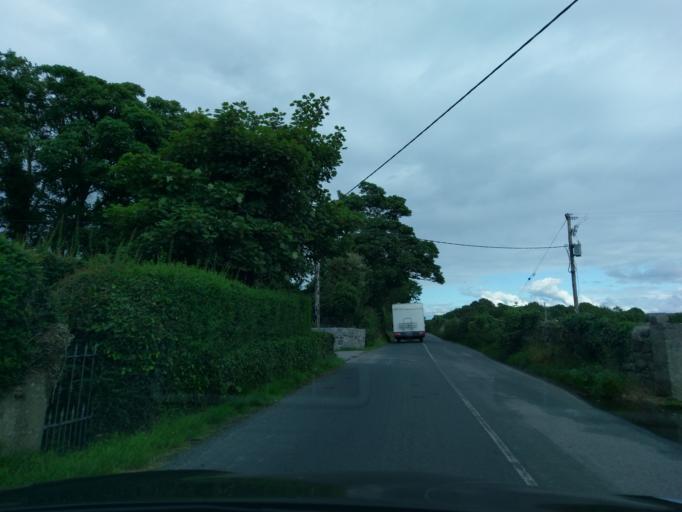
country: IE
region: Connaught
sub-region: County Galway
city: Gort
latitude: 53.1642
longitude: -8.7870
